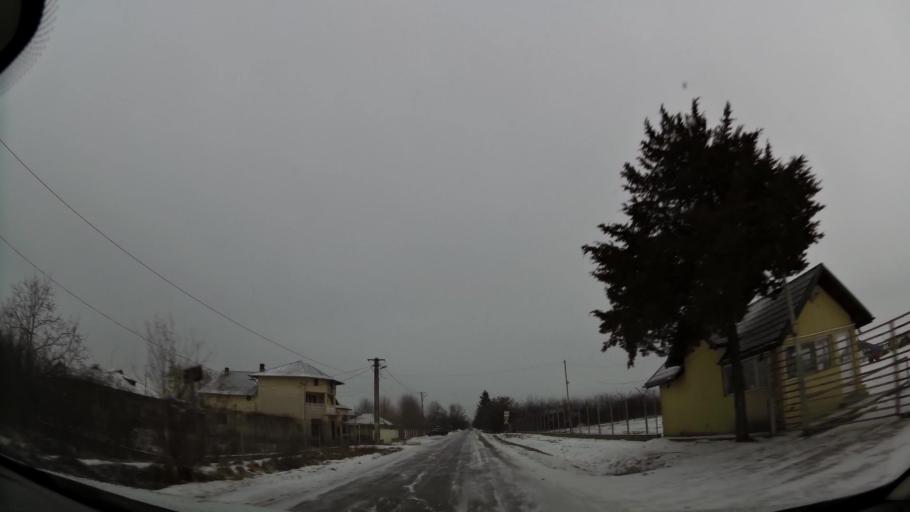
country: RO
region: Prahova
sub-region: Comuna Poenarii-Burchi
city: Ologeni
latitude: 44.7332
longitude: 25.9360
